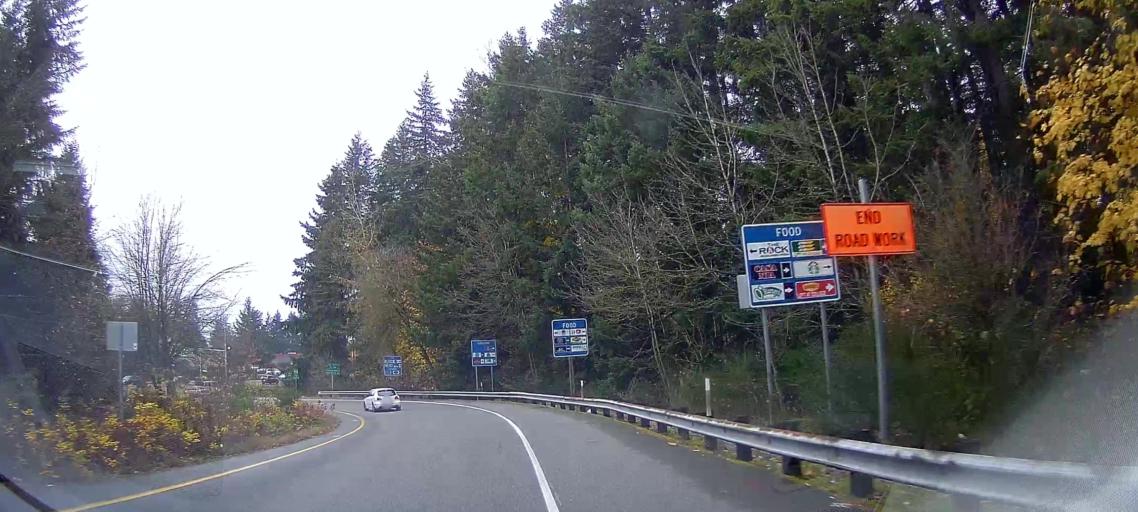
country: US
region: Washington
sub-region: Thurston County
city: Lacey
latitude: 47.0496
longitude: -122.8193
